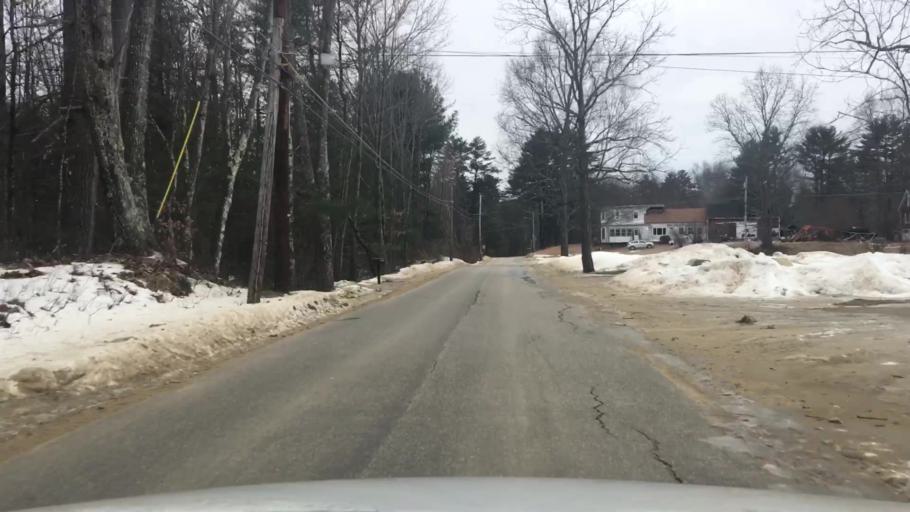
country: US
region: New Hampshire
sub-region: Strafford County
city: Rochester
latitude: 43.3467
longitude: -70.9608
